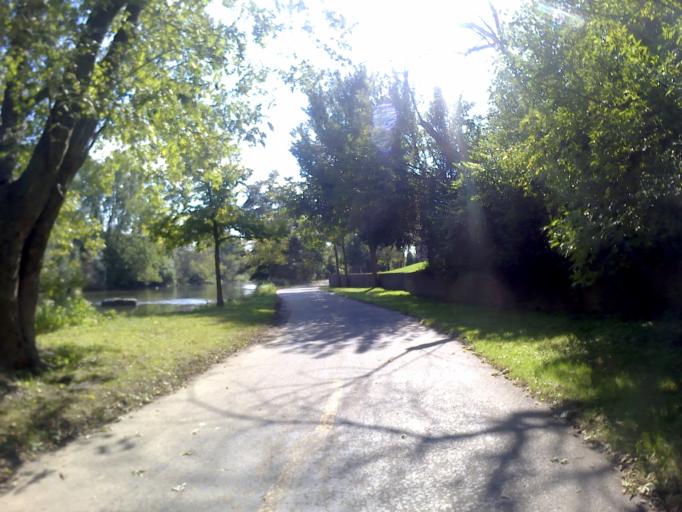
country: US
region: Illinois
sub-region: DuPage County
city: Naperville
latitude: 41.7379
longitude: -88.1269
